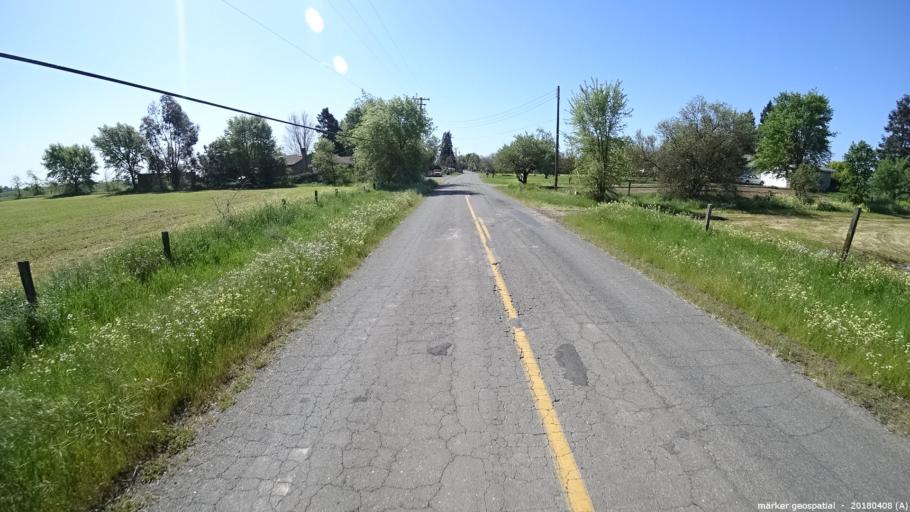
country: US
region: California
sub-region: Sacramento County
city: Laguna
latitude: 38.3359
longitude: -121.4637
